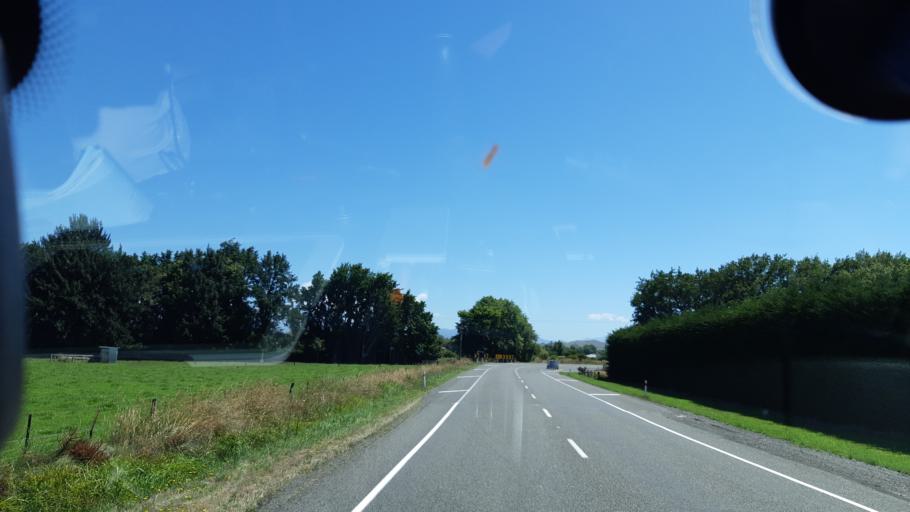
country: NZ
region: Canterbury
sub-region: Kaikoura District
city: Kaikoura
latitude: -42.7409
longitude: 173.2666
